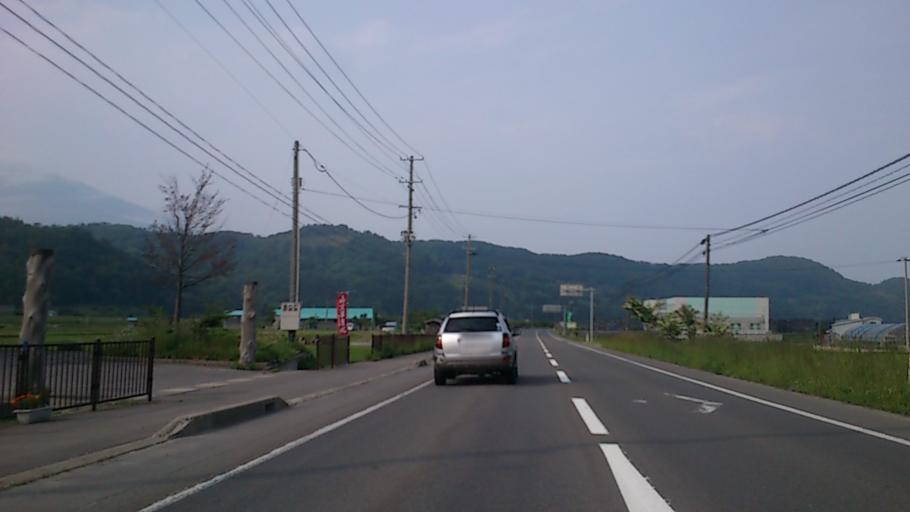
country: JP
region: Aomori
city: Hirosaki
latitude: 40.5798
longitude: 140.3013
